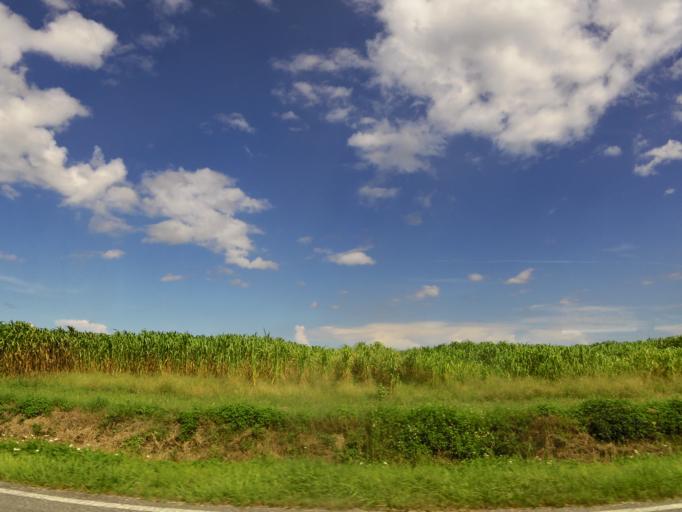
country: US
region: Florida
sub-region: Saint Johns County
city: Saint Augustine Shores
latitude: 29.8032
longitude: -81.4845
